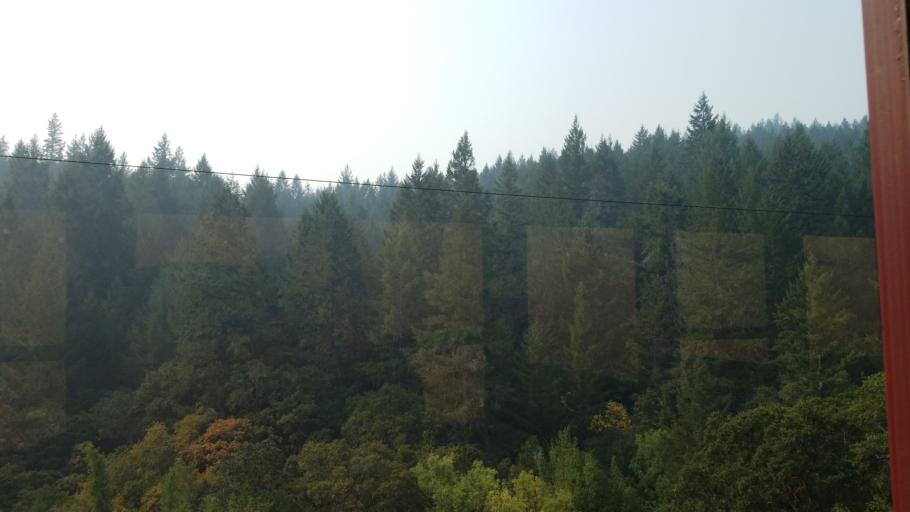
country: US
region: California
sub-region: Mendocino County
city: Willits
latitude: 39.4028
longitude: -123.3951
